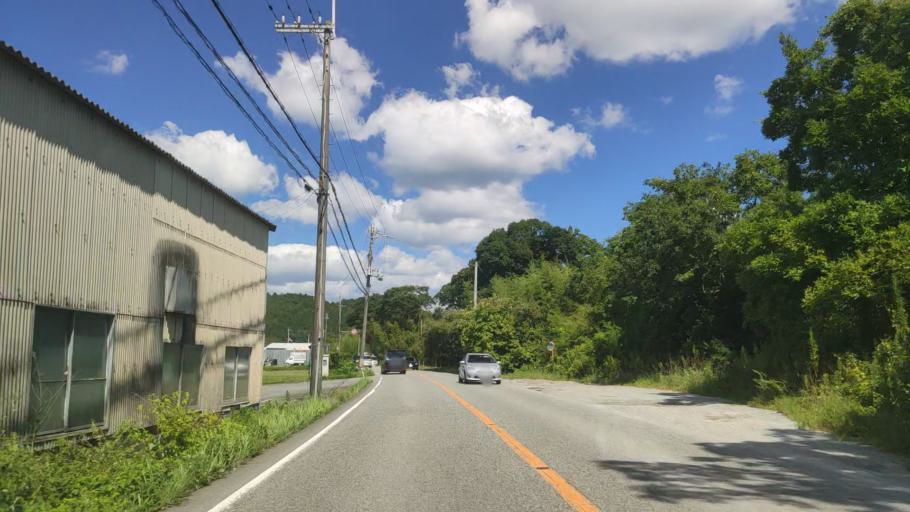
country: JP
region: Kyoto
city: Fukuchiyama
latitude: 35.1834
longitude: 135.1235
